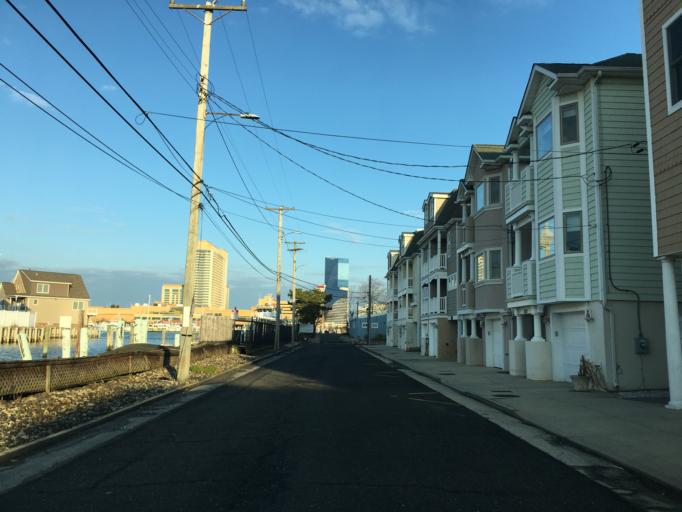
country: US
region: New Jersey
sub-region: Atlantic County
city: Atlantic City
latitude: 39.3753
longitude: -74.4231
